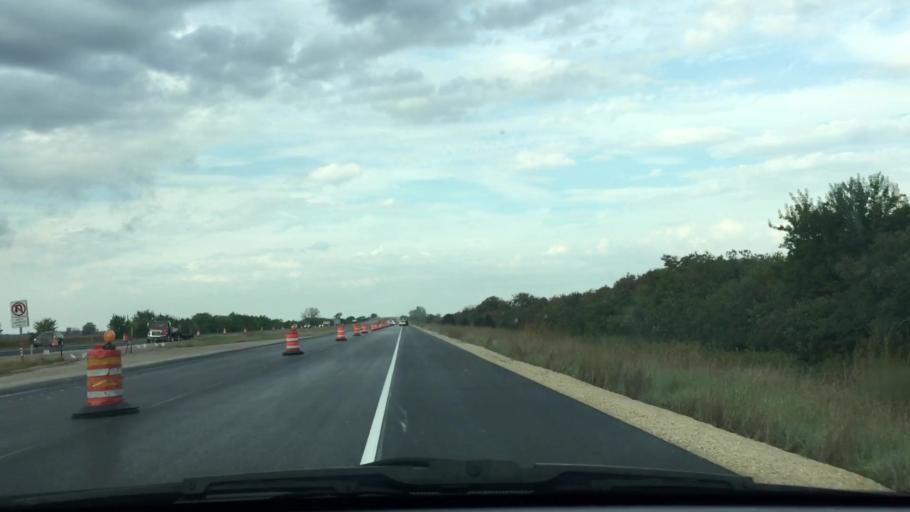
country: US
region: Illinois
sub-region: Whiteside County
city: Prophetstown
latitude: 41.7186
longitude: -89.9834
